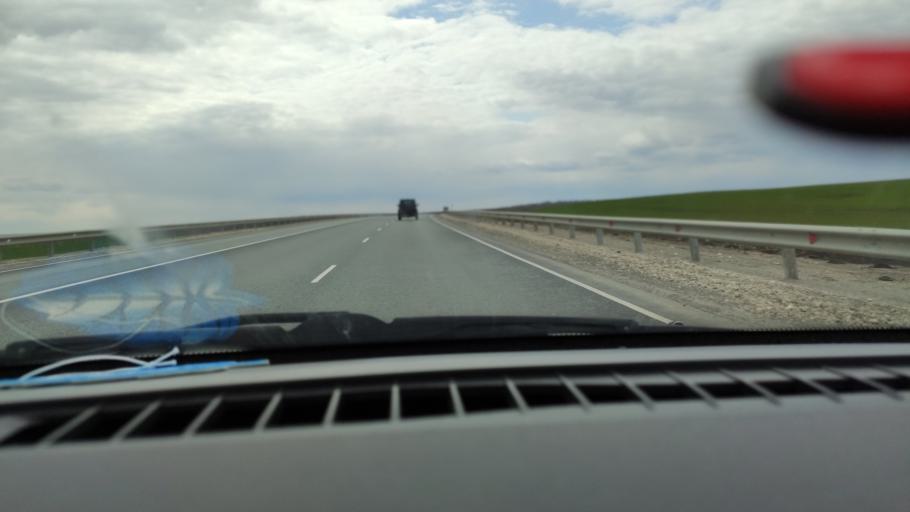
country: RU
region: Saratov
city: Yelshanka
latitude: 51.8327
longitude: 46.4629
